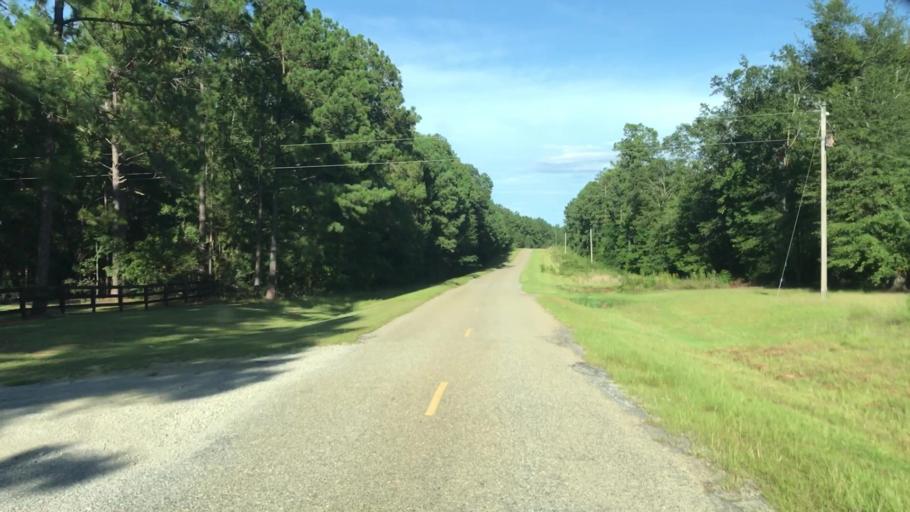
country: US
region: Georgia
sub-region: Jefferson County
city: Wadley
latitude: 32.8095
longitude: -82.3346
